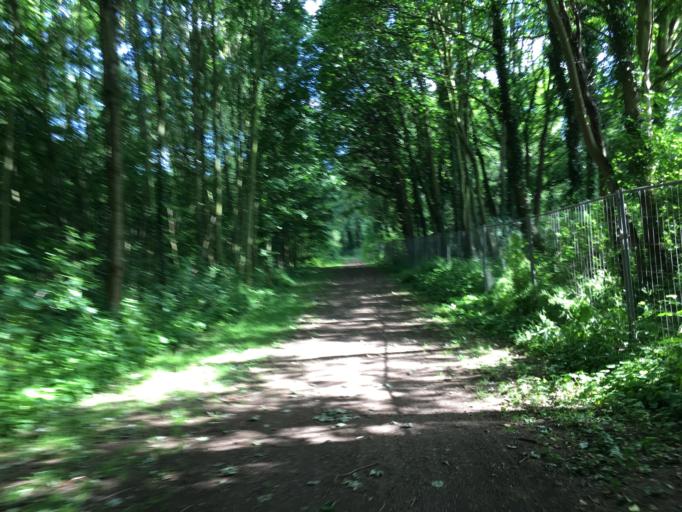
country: DE
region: North Rhine-Westphalia
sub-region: Regierungsbezirk Koln
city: Dueren
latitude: 50.7829
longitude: 6.4723
